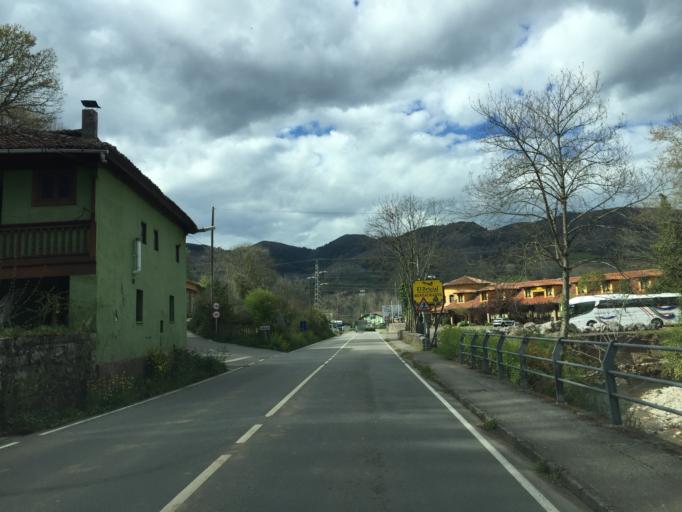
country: ES
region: Asturias
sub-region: Province of Asturias
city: Cangas de Onis
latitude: 43.3449
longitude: -5.0847
